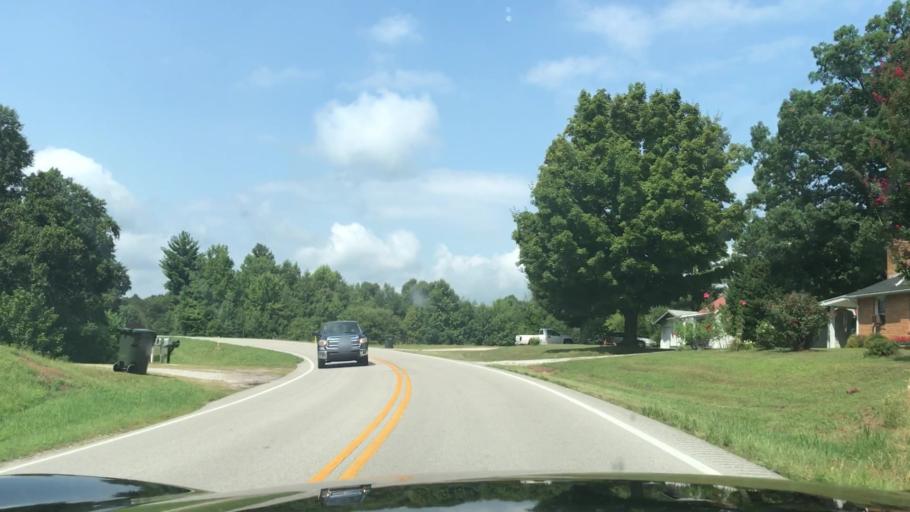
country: US
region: Kentucky
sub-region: Butler County
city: Morgantown
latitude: 37.1812
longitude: -86.8627
